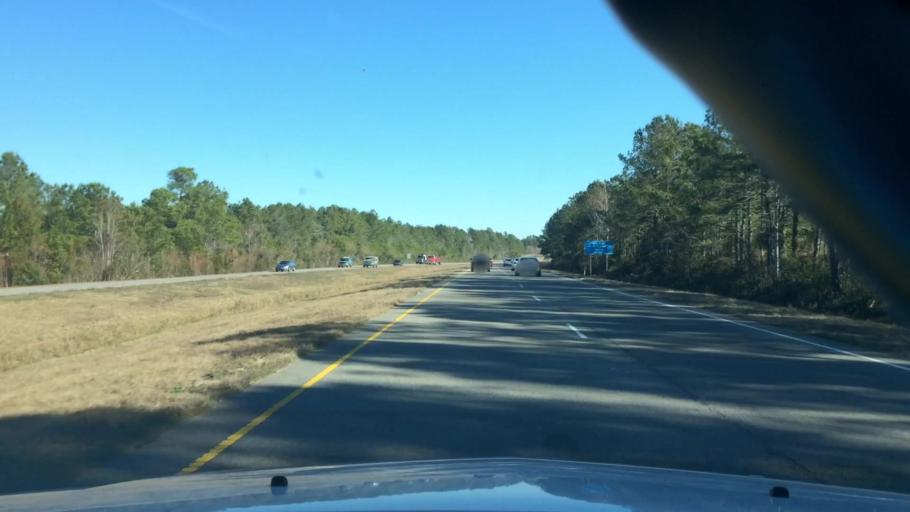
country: US
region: North Carolina
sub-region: Brunswick County
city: Shallotte
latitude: 33.9691
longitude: -78.4120
